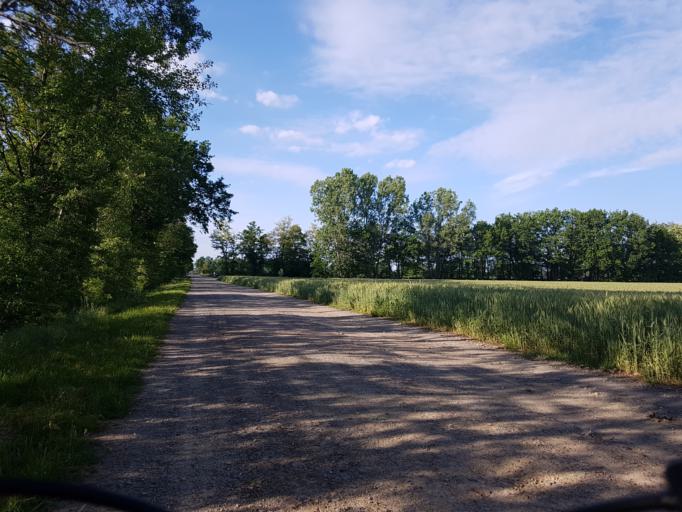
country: DE
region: Brandenburg
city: Elsterwerda
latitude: 51.4326
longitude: 13.5299
